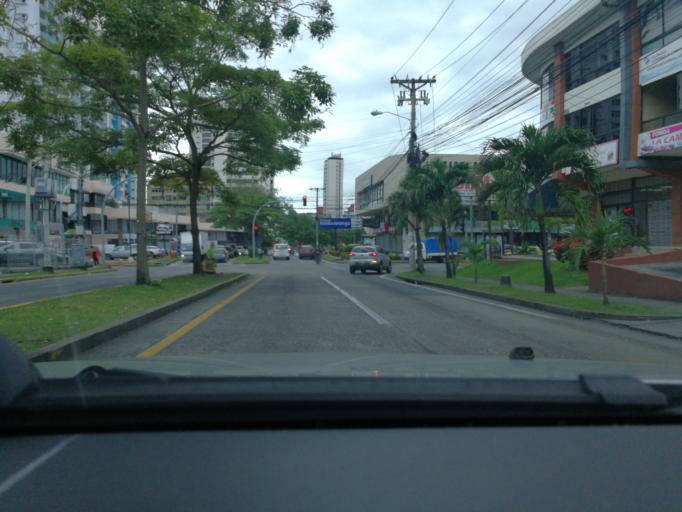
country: PA
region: Panama
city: Panama
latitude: 9.0069
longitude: -79.5358
